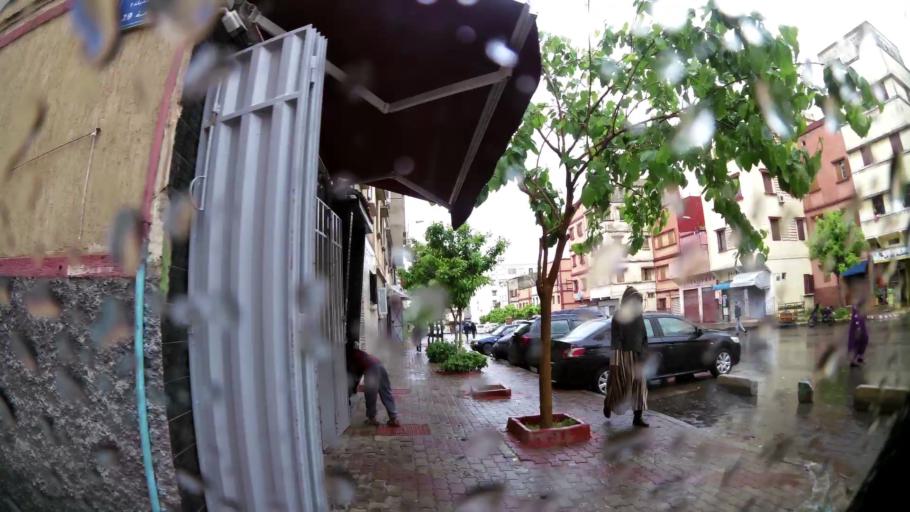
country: MA
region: Grand Casablanca
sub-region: Casablanca
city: Casablanca
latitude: 33.5474
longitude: -7.5795
